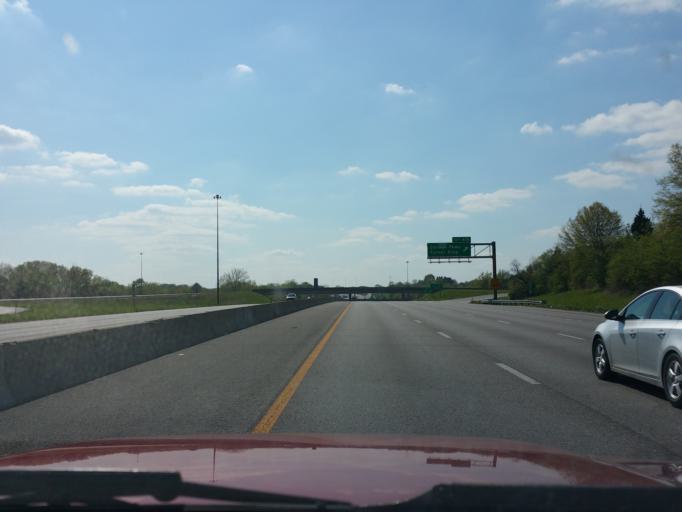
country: US
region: Kansas
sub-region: Johnson County
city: Shawnee
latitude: 39.1061
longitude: -94.7327
